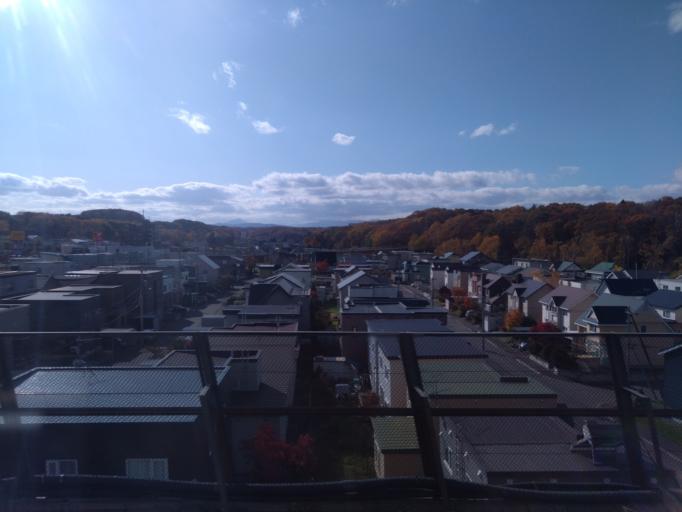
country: JP
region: Hokkaido
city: Kitahiroshima
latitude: 42.9867
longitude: 141.5611
